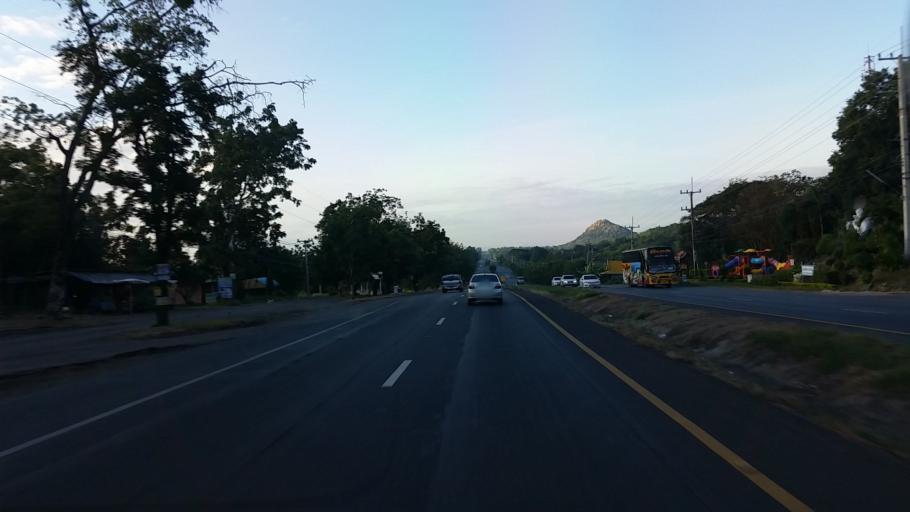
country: TH
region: Lop Buri
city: Chai Badan
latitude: 15.1547
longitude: 101.0555
